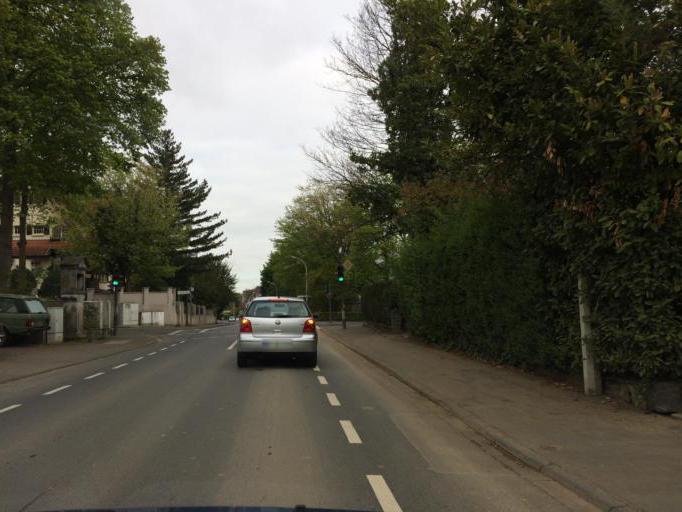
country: DE
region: North Rhine-Westphalia
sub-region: Regierungsbezirk Koln
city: Konigswinter
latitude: 50.6714
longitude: 7.1642
